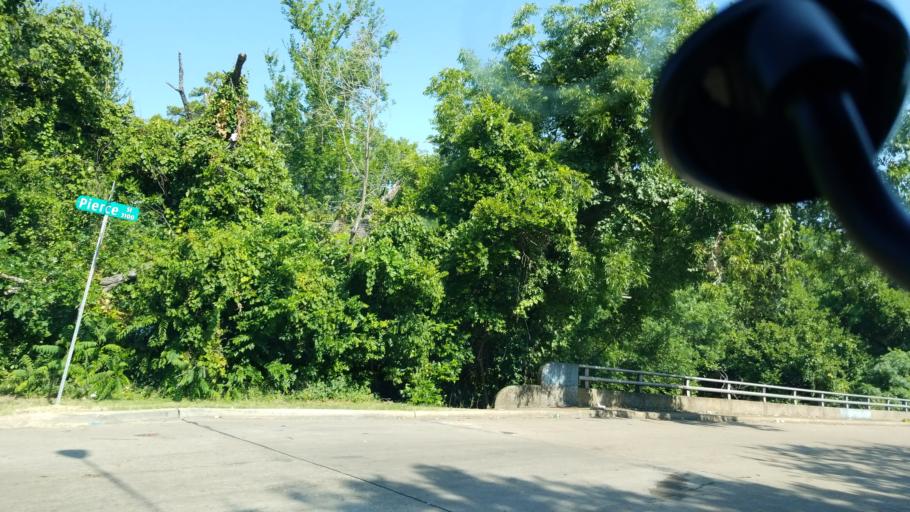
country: US
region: Texas
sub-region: Dallas County
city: Cockrell Hill
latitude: 32.7050
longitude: -96.8658
